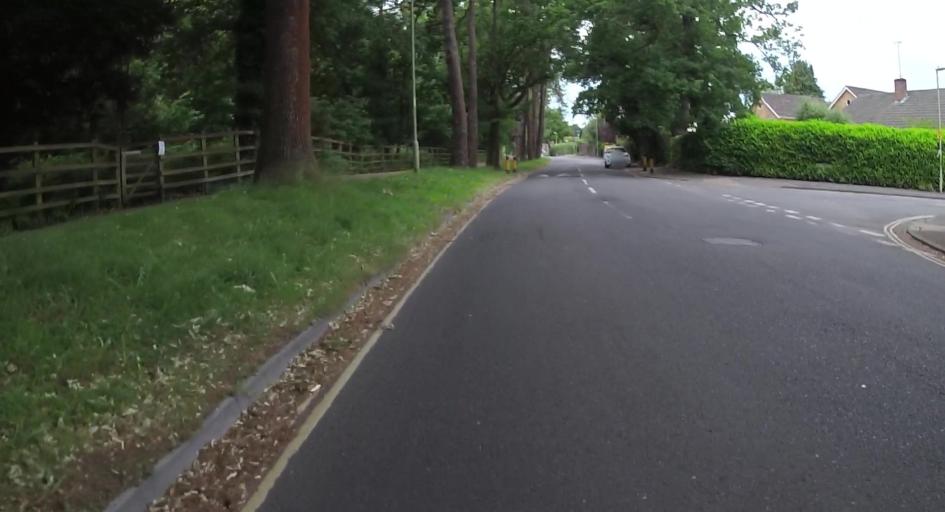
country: GB
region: England
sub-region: Hampshire
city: Fleet
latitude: 51.2586
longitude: -0.8334
